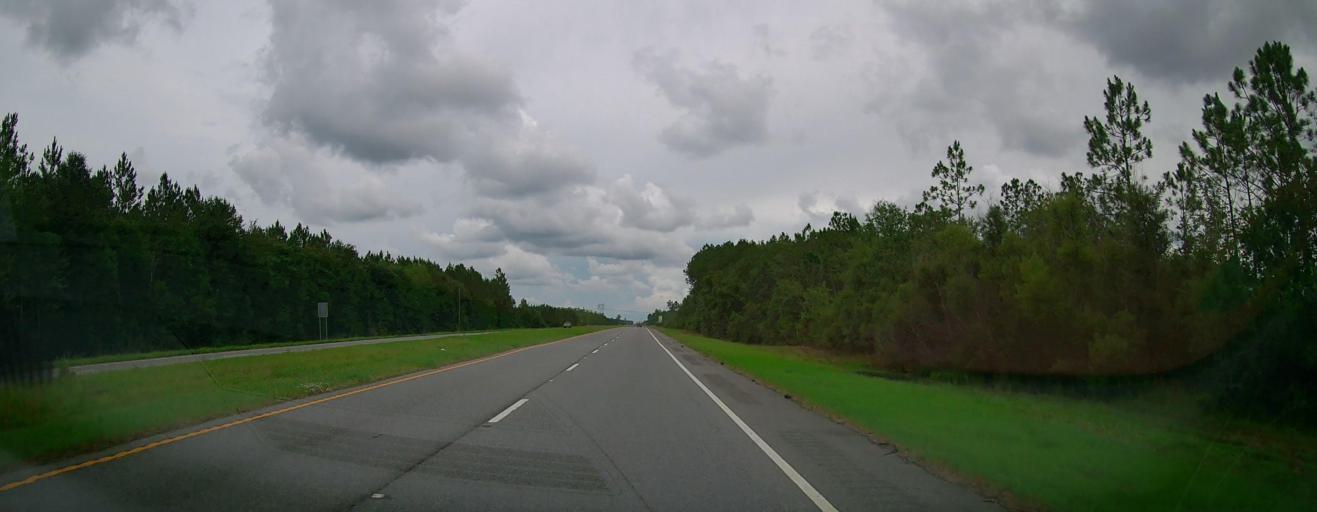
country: US
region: Georgia
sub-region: Wayne County
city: Jesup
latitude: 31.6821
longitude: -82.0963
